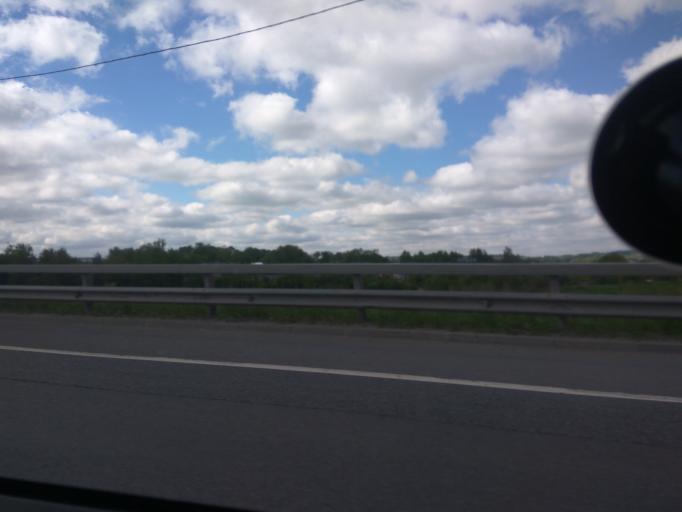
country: RU
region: Moskovskaya
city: Zhukovskiy
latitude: 55.5753
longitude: 38.0995
